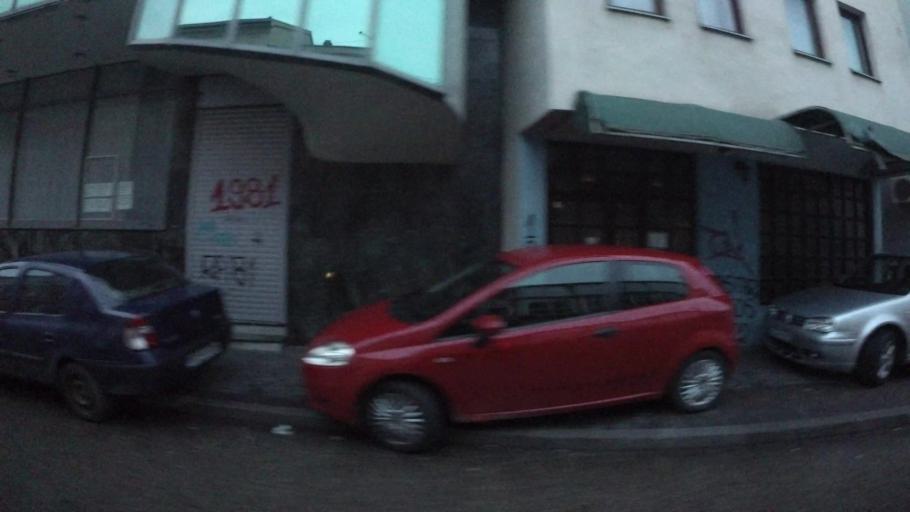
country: BA
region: Federation of Bosnia and Herzegovina
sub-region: Hercegovacko-Bosanski Kanton
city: Mostar
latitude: 43.3349
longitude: 17.8172
